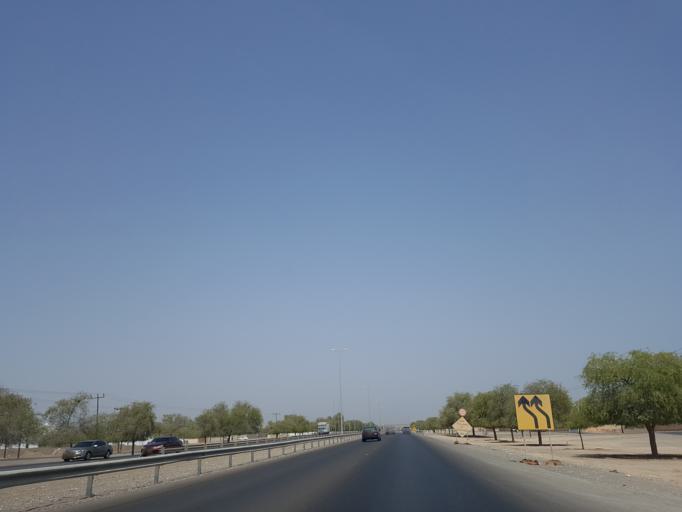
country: OM
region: Al Batinah
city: Saham
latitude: 24.0608
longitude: 56.9625
